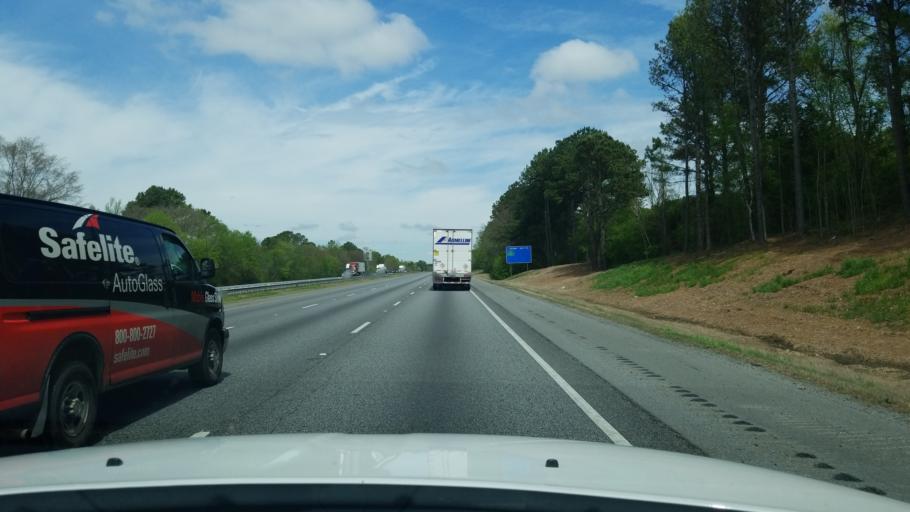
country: US
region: Georgia
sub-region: Gordon County
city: Calhoun
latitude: 34.4854
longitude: -84.9196
